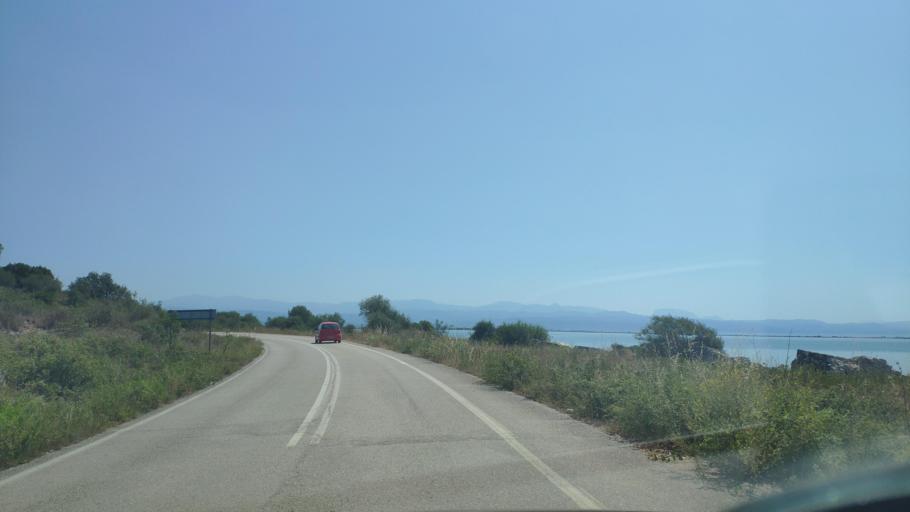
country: GR
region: Epirus
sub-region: Nomos Artas
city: Aneza
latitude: 39.0316
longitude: 20.8706
